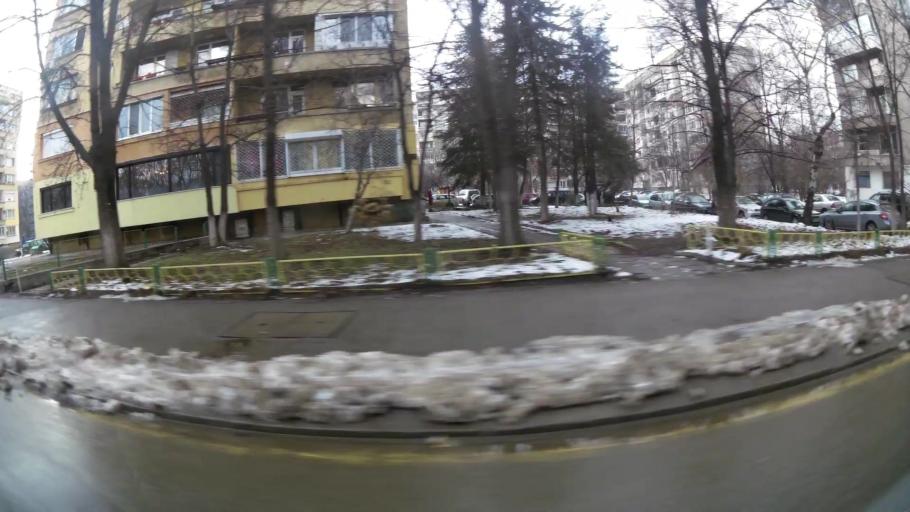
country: BG
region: Sofia-Capital
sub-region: Stolichna Obshtina
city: Sofia
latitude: 42.7055
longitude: 23.2968
